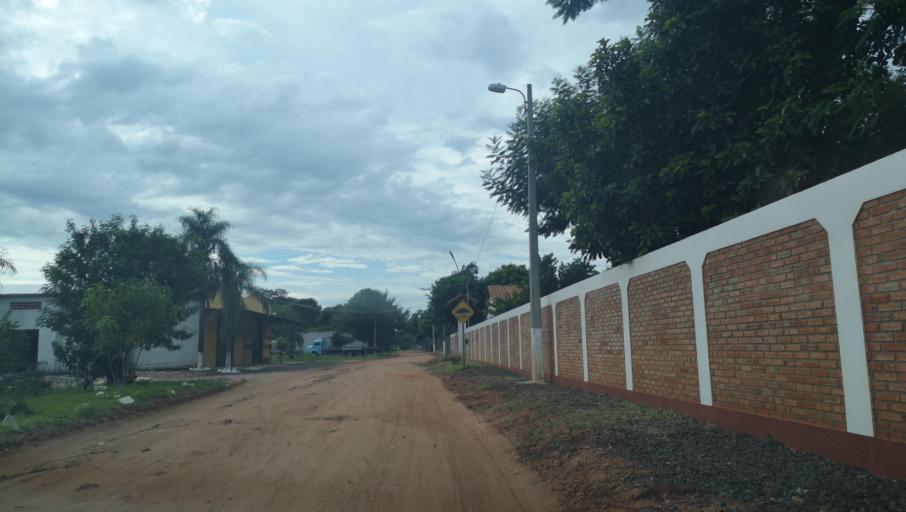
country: PY
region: San Pedro
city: Capiibary
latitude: -24.7322
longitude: -56.0252
